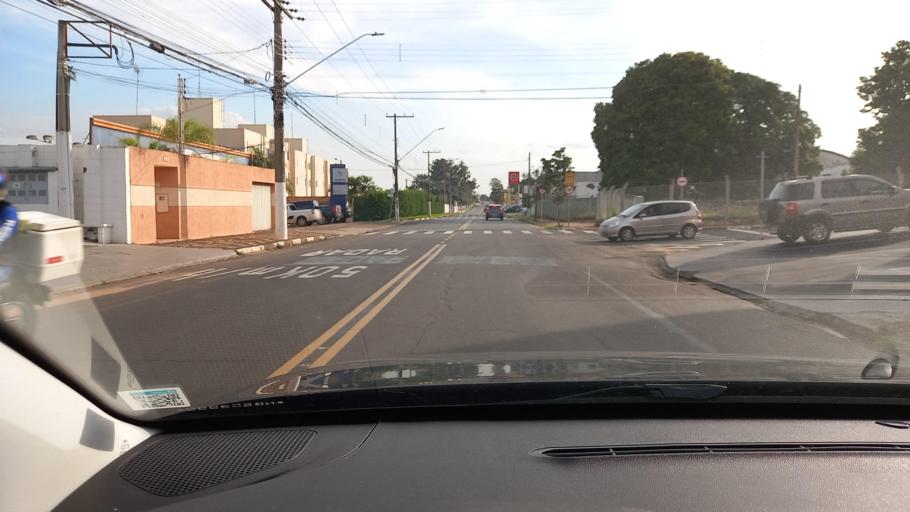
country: BR
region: Sao Paulo
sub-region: Mogi-Mirim
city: Mogi Mirim
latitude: -22.4445
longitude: -46.9735
